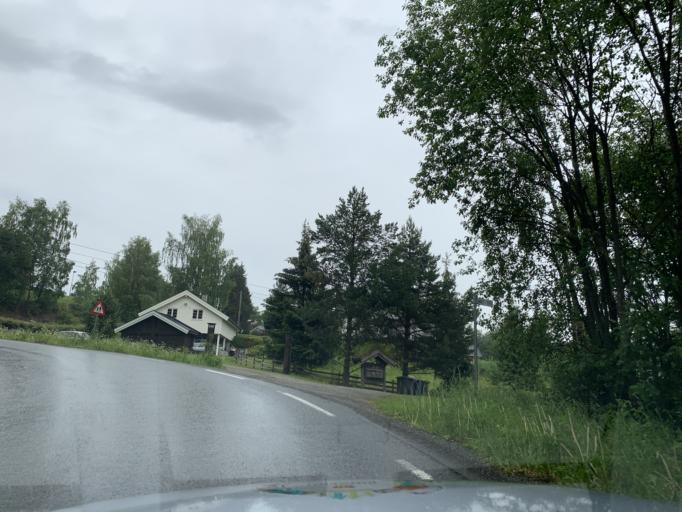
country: NO
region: Oppland
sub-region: Ringebu
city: Ringebu
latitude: 61.4439
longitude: 10.1832
